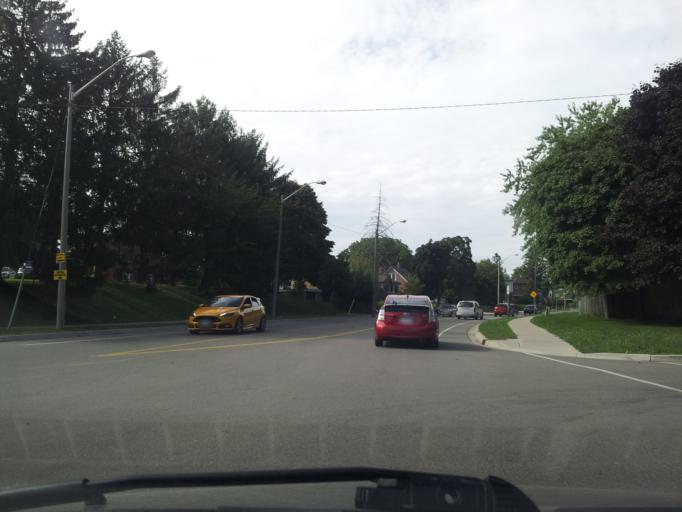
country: CA
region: Ontario
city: Kitchener
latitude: 43.4338
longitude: -80.4743
